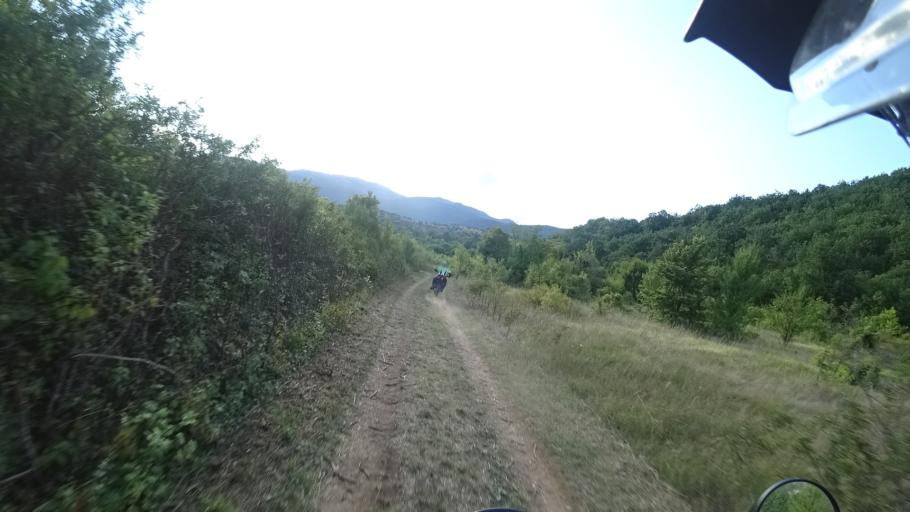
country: HR
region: Sibensko-Kniniska
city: Knin
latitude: 44.2041
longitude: 16.0752
